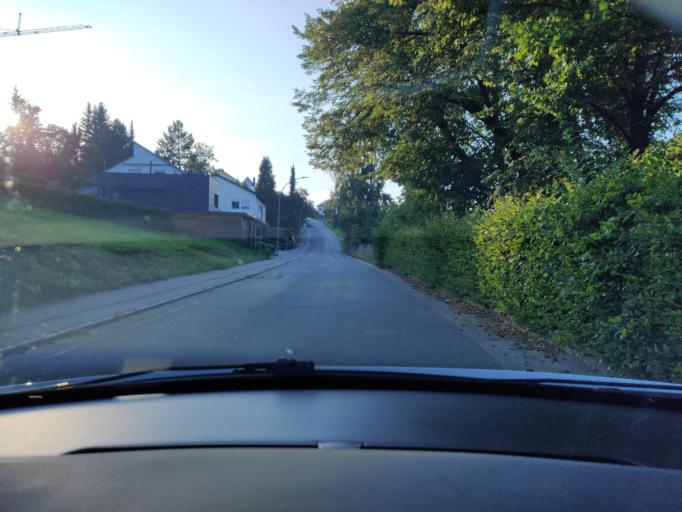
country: DE
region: Bavaria
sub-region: Upper Palatinate
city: Nabburg
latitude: 49.4531
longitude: 12.1773
